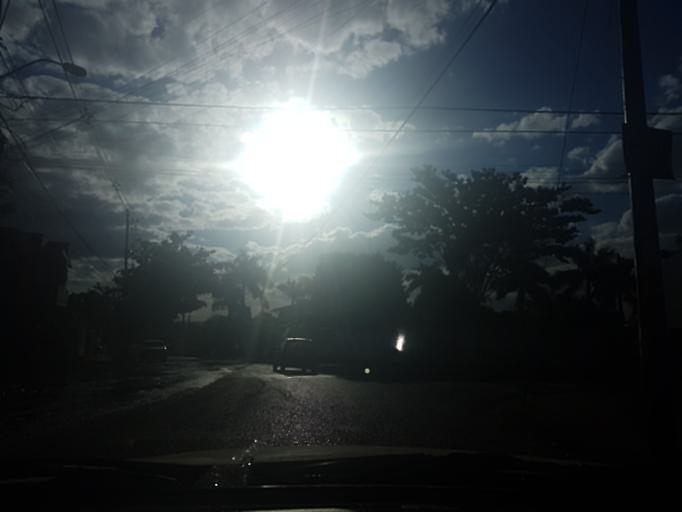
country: PY
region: Asuncion
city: Asuncion
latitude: -25.2678
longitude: -57.5805
